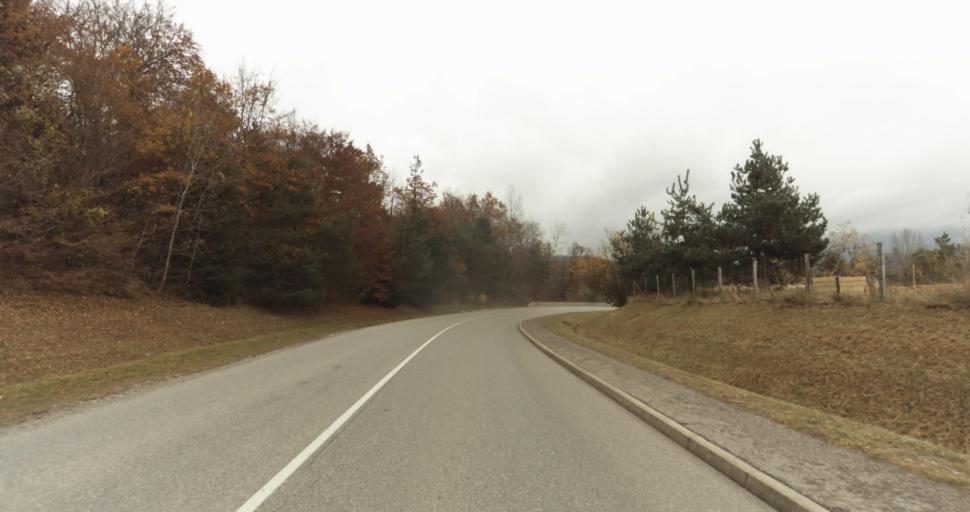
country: FR
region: Rhone-Alpes
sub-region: Departement de la Haute-Savoie
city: Groisy
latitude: 46.0053
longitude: 6.1800
